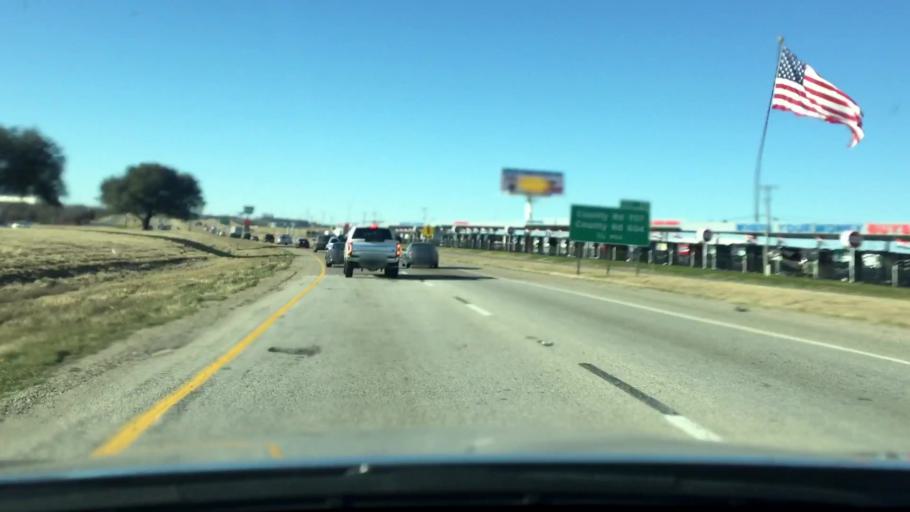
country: US
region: Texas
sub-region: Johnson County
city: Alvarado
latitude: 32.4217
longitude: -97.2291
